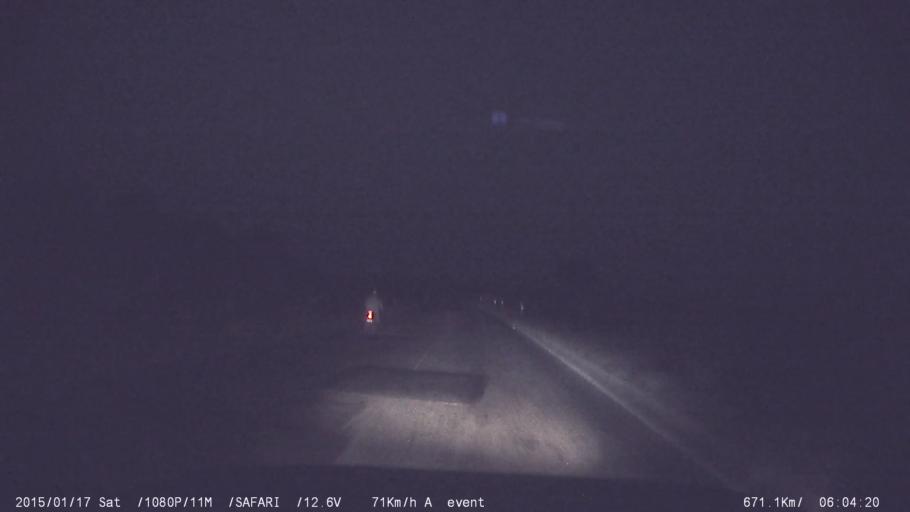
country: IN
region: Tamil Nadu
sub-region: Kancheepuram
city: Kanchipuram
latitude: 12.8760
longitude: 79.6145
